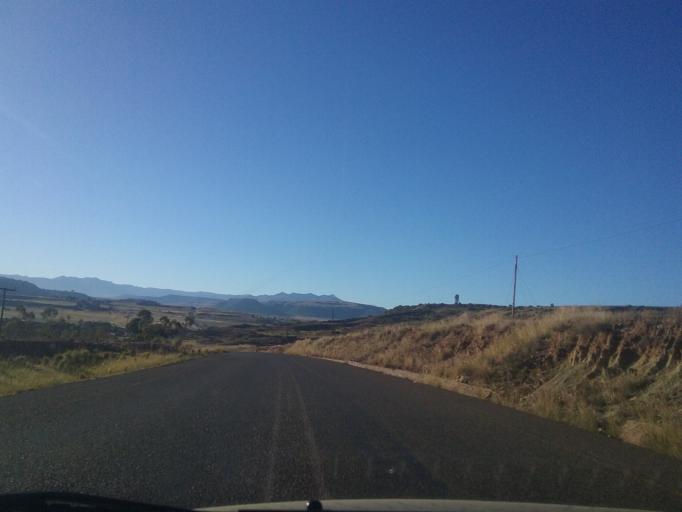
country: LS
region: Quthing
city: Quthing
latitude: -30.3702
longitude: 27.5552
